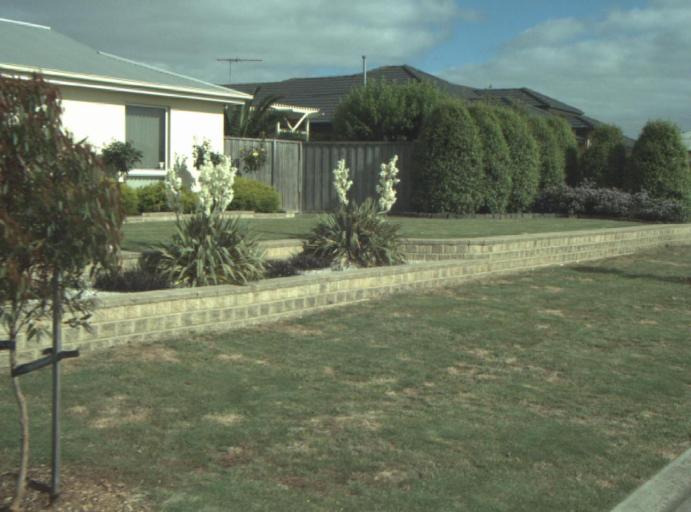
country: AU
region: Victoria
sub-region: Greater Geelong
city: Wandana Heights
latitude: -38.2131
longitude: 144.2980
